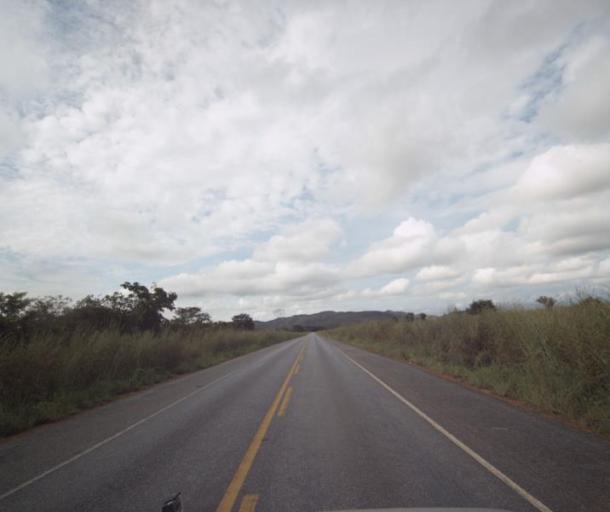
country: BR
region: Goias
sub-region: Pirenopolis
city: Pirenopolis
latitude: -15.5614
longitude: -48.6223
